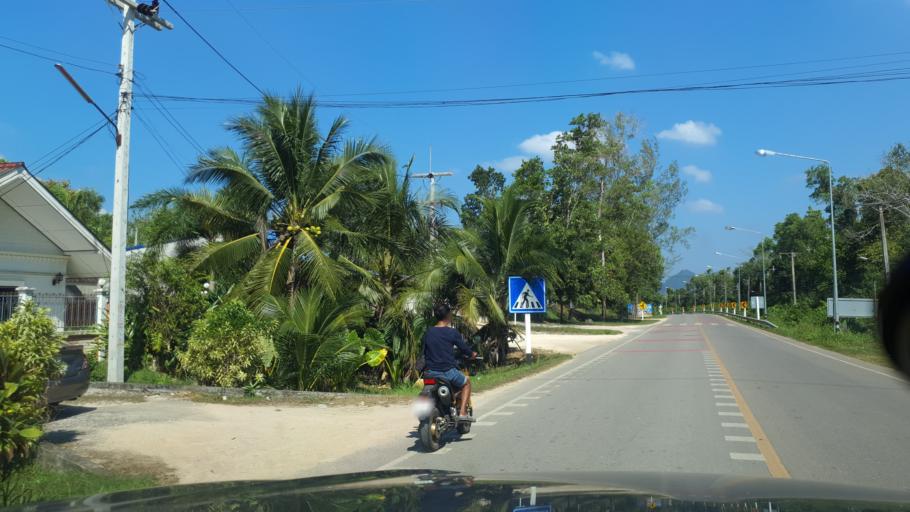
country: TH
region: Phangnga
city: Ban Ao Nang
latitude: 8.0420
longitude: 98.8614
